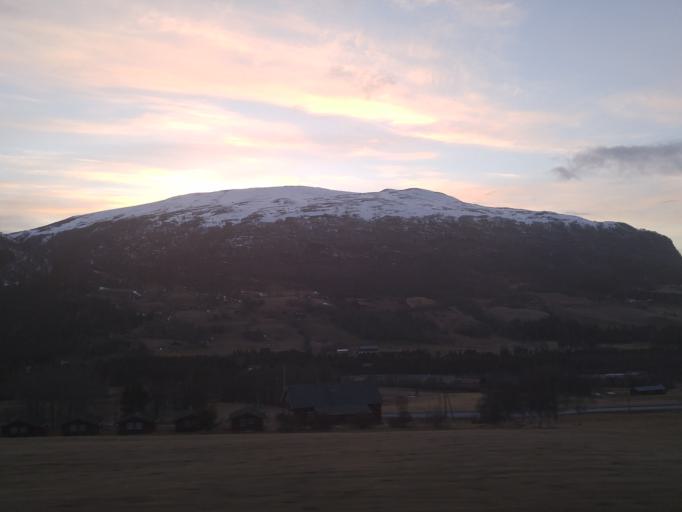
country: NO
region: Sor-Trondelag
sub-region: Oppdal
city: Oppdal
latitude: 62.5287
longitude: 9.6160
